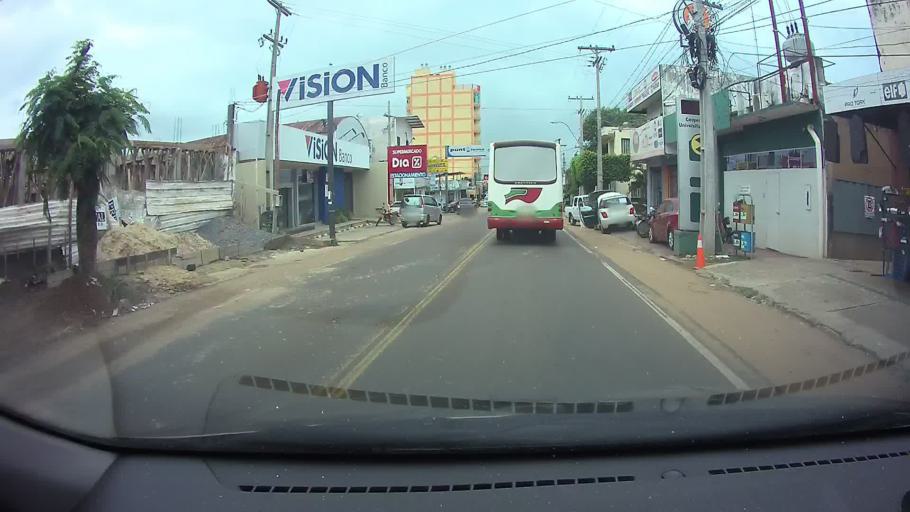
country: PY
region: Paraguari
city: Carapegua
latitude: -25.7676
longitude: -57.2394
